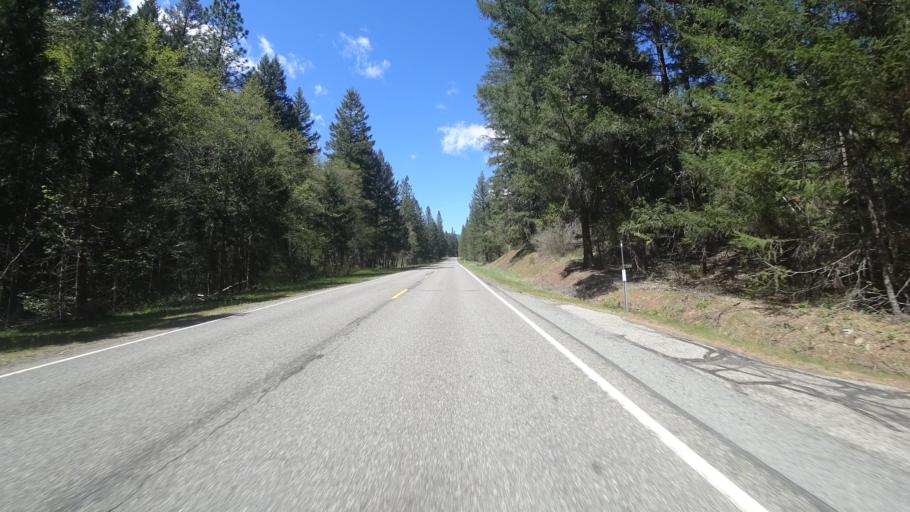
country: US
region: California
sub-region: Trinity County
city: Weaverville
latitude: 40.7734
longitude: -122.8920
